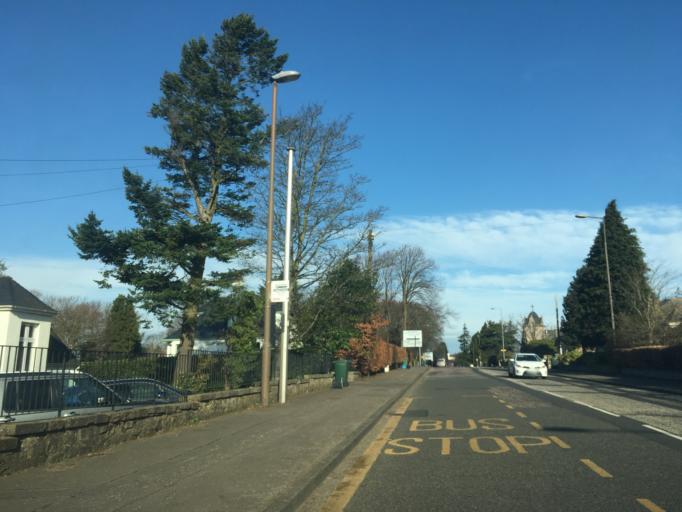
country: GB
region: Scotland
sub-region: Midlothian
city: Loanhead
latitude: 55.9004
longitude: -3.2012
